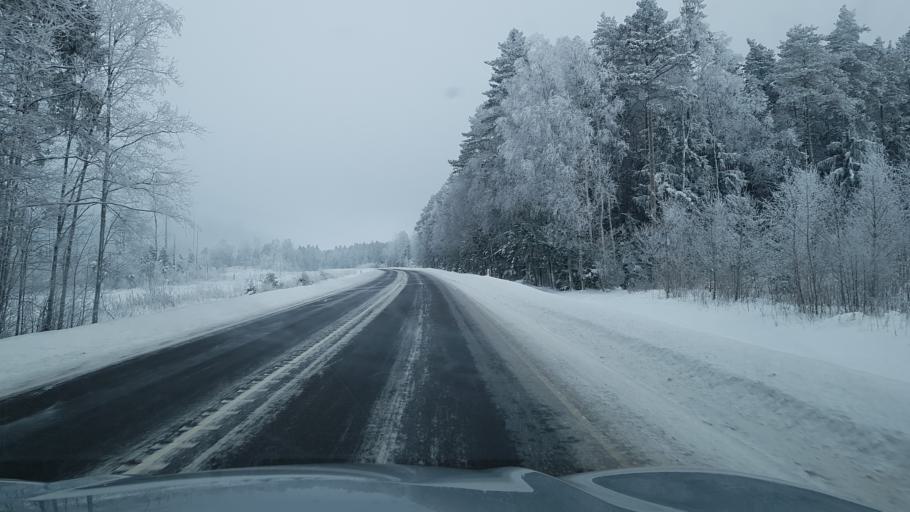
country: EE
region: Ida-Virumaa
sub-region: Johvi vald
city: Johvi
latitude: 59.2884
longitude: 27.3988
